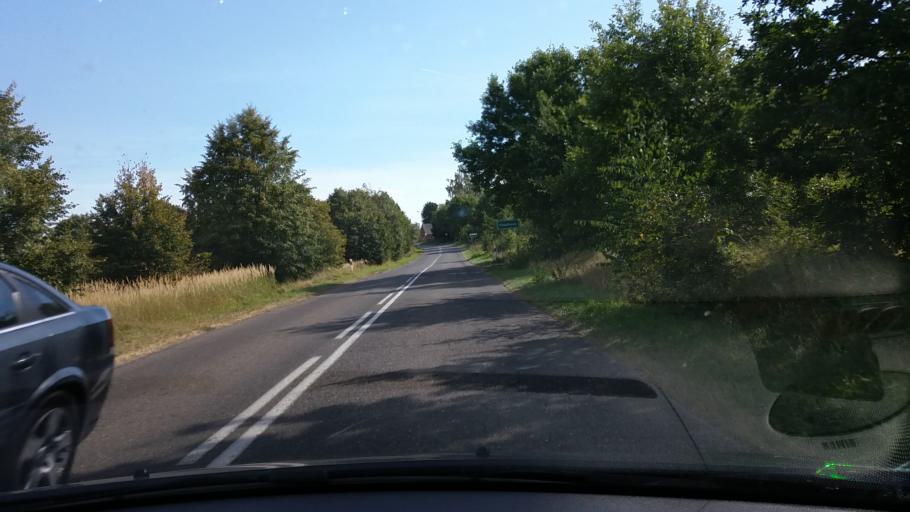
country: PL
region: Lubusz
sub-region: Powiat strzelecko-drezdenecki
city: Dobiegniew
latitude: 53.0120
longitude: 15.7328
